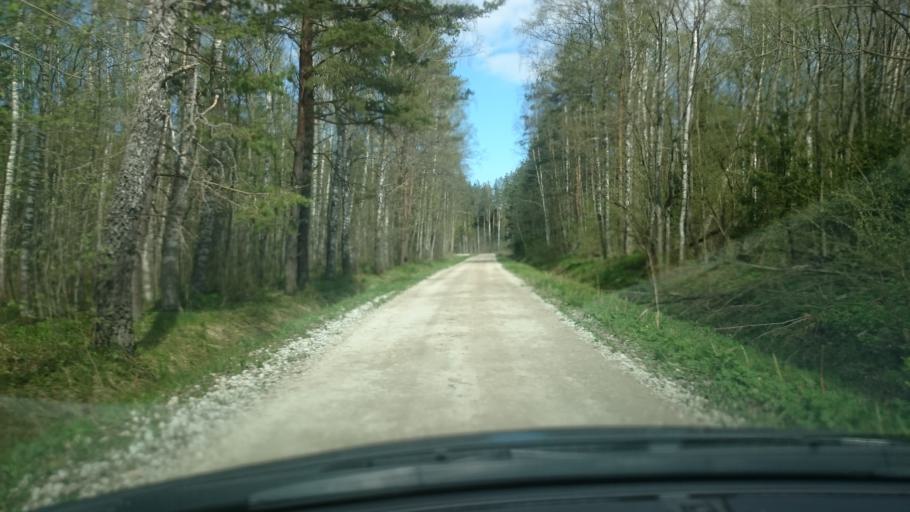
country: EE
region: Ida-Virumaa
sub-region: Sillamaee linn
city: Sillamae
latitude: 59.1432
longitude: 27.8083
